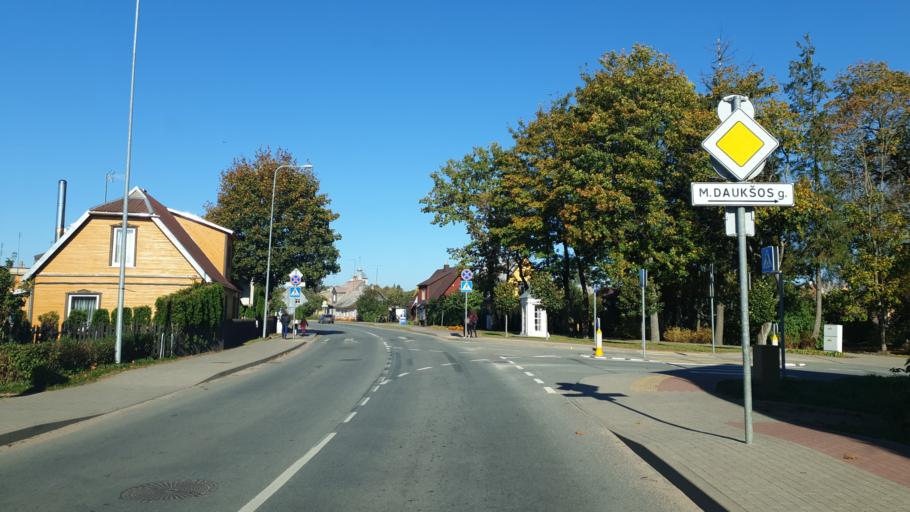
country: LT
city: Varniai
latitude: 55.7394
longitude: 22.3769
